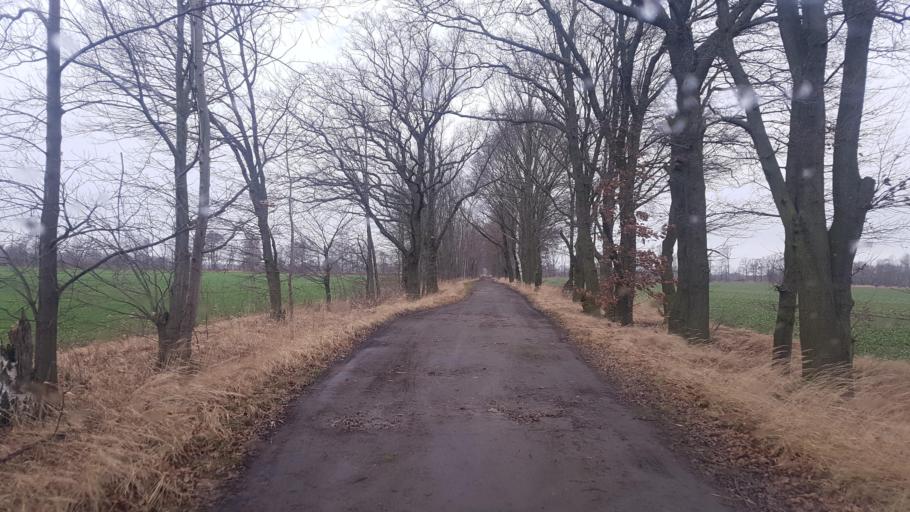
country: DE
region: Brandenburg
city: Grossthiemig
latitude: 51.4260
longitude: 13.6562
